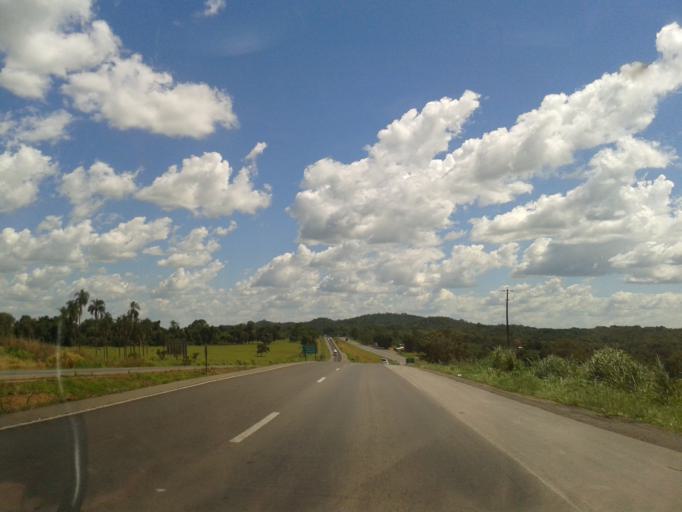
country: BR
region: Goias
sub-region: Piracanjuba
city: Piracanjuba
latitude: -17.3239
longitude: -49.2392
